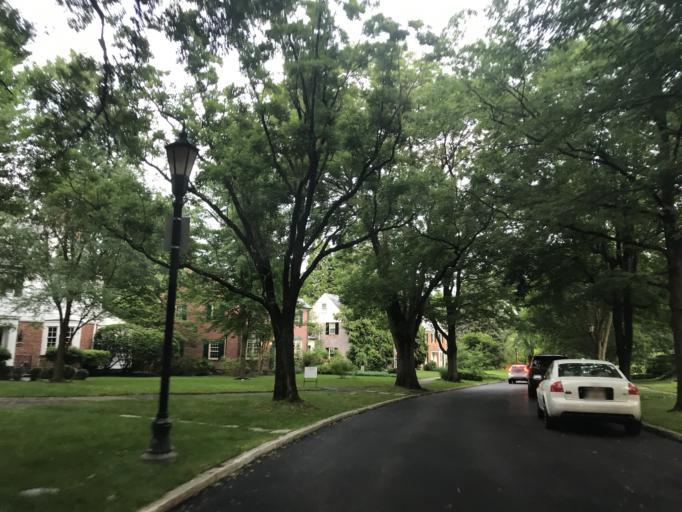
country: US
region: Maryland
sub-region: Baltimore County
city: Towson
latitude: 39.3628
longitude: -76.6192
